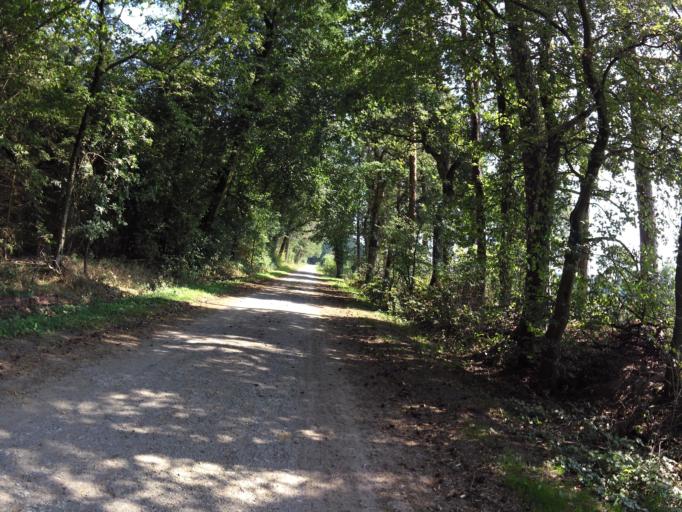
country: DE
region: North Rhine-Westphalia
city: Stadtlohn
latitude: 52.0113
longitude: 6.9734
